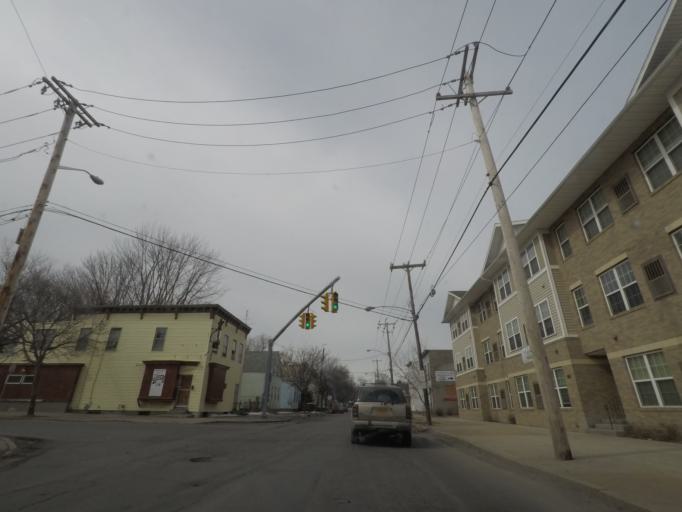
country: US
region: New York
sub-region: Albany County
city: West Albany
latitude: 42.6709
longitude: -73.7710
